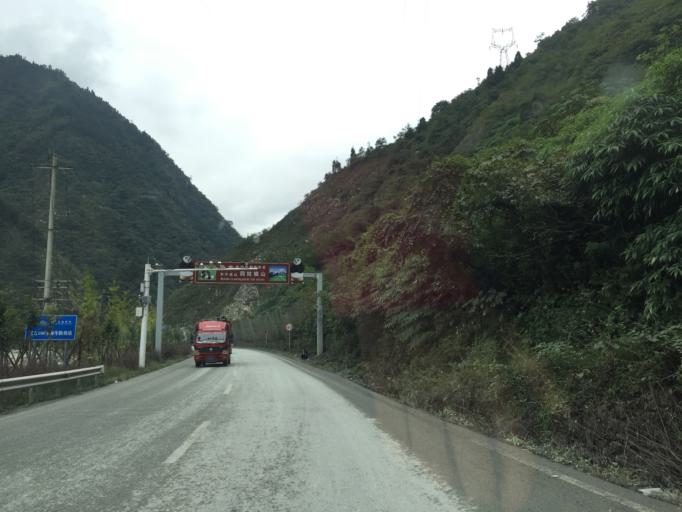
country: CN
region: Sichuan
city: Guangsheng
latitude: 31.0661
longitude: 103.4830
